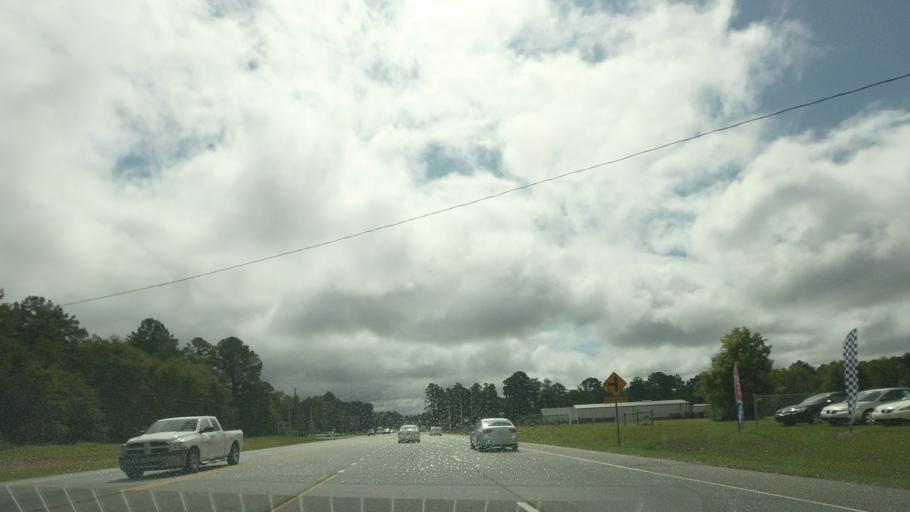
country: US
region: Georgia
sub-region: Laurens County
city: Dublin
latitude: 32.5479
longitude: -82.9691
